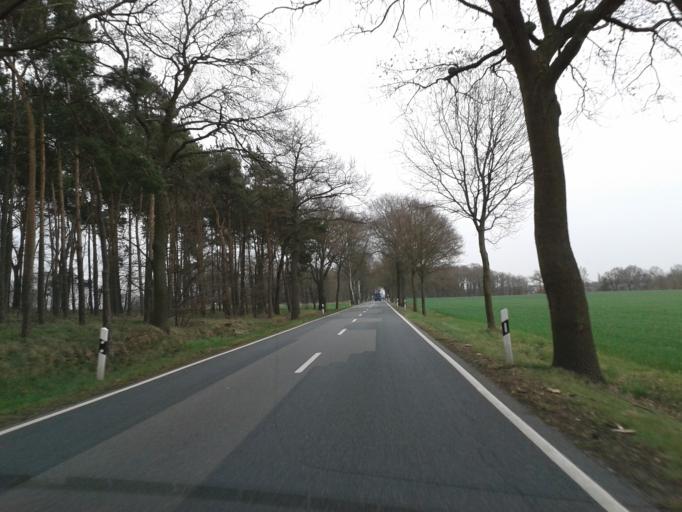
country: DE
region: Lower Saxony
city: Prezelle
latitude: 52.9096
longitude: 11.3304
